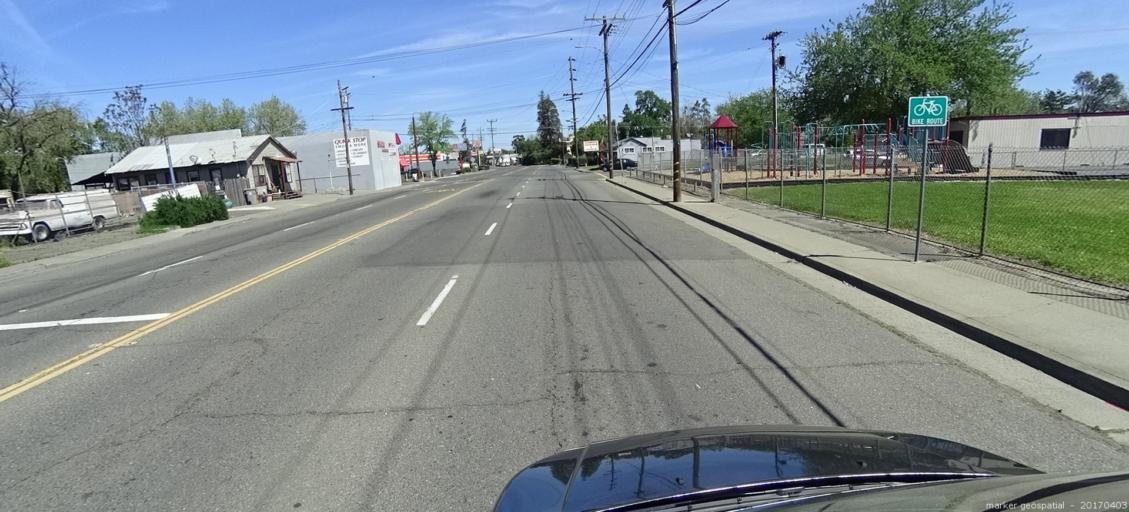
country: US
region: California
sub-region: Sacramento County
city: Arden-Arcade
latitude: 38.6230
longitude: -121.4347
